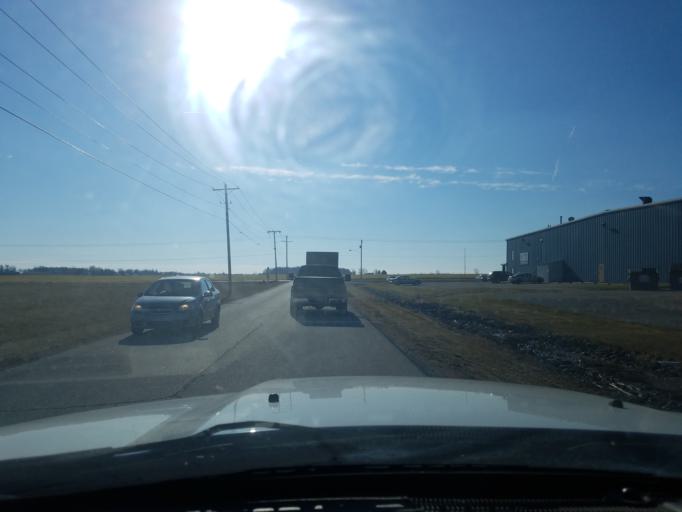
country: US
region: Indiana
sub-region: Wells County
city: Ossian
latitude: 40.8674
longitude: -85.1728
